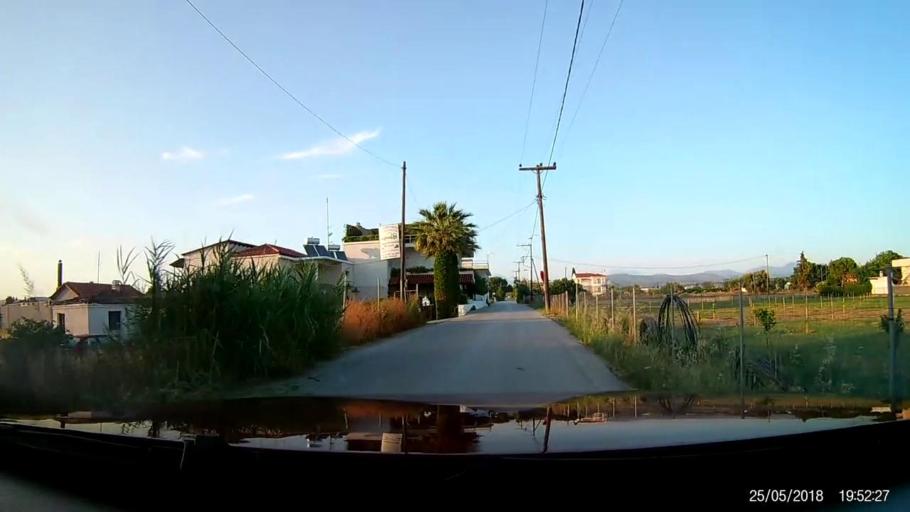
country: GR
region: Central Greece
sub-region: Nomos Evvoias
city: Ayios Nikolaos
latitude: 38.4111
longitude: 23.6454
